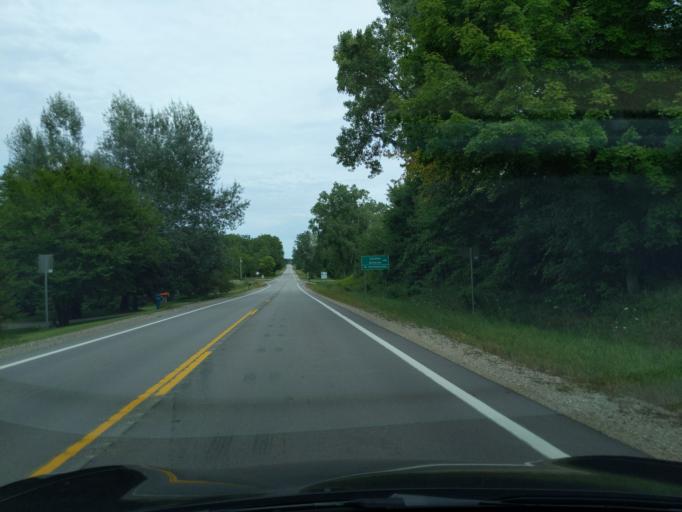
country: US
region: Michigan
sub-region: Barry County
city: Nashville
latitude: 42.5673
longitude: -85.0168
